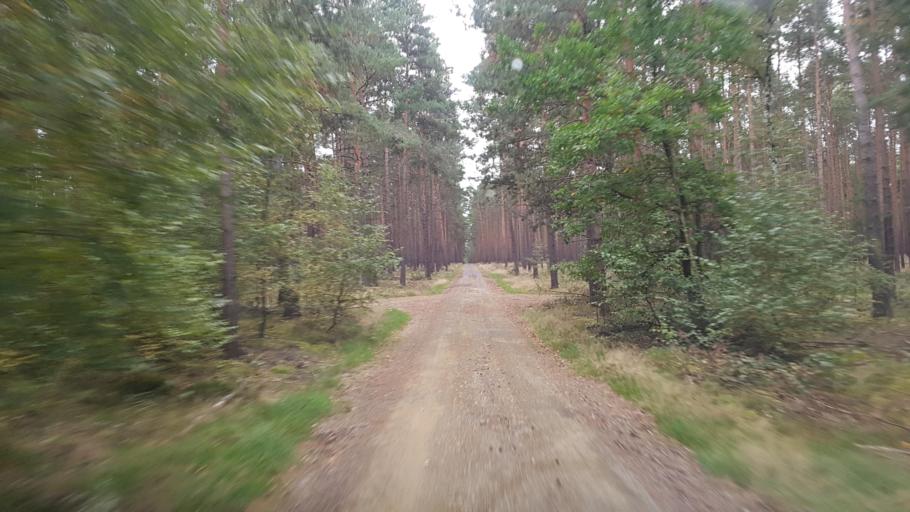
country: DE
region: Brandenburg
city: Sonnewalde
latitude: 51.7310
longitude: 13.6618
